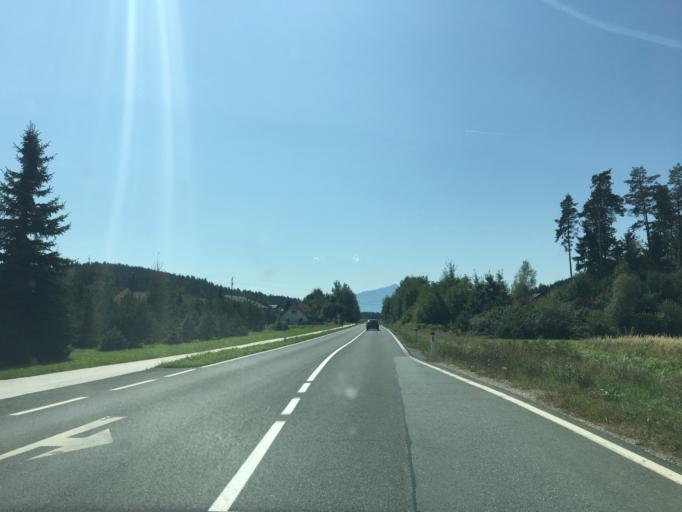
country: AT
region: Carinthia
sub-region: Politischer Bezirk Volkermarkt
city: Voelkermarkt
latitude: 46.6739
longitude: 14.6681
